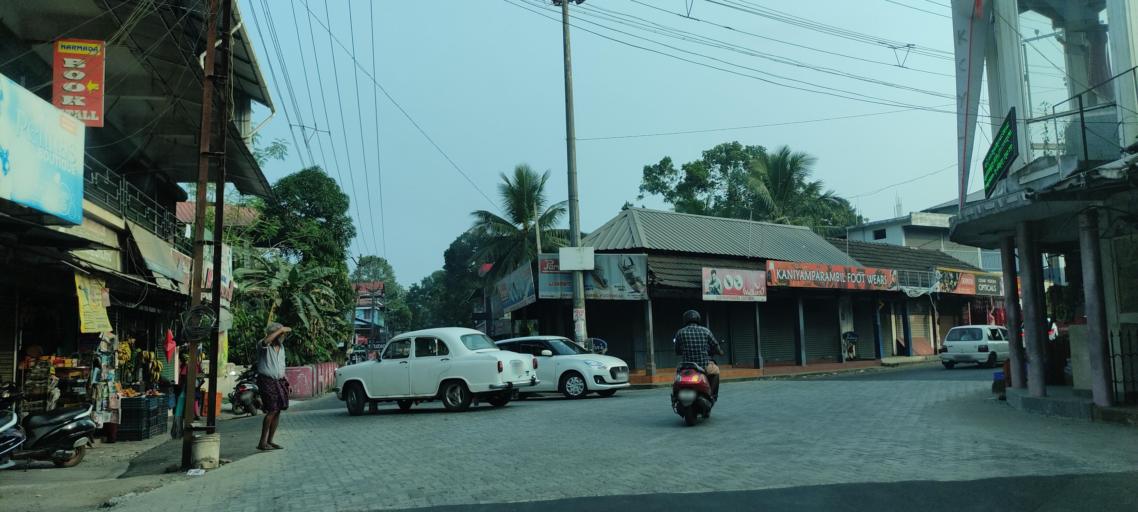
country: IN
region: Kerala
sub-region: Kottayam
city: Vaikam
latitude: 9.6981
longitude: 76.4779
